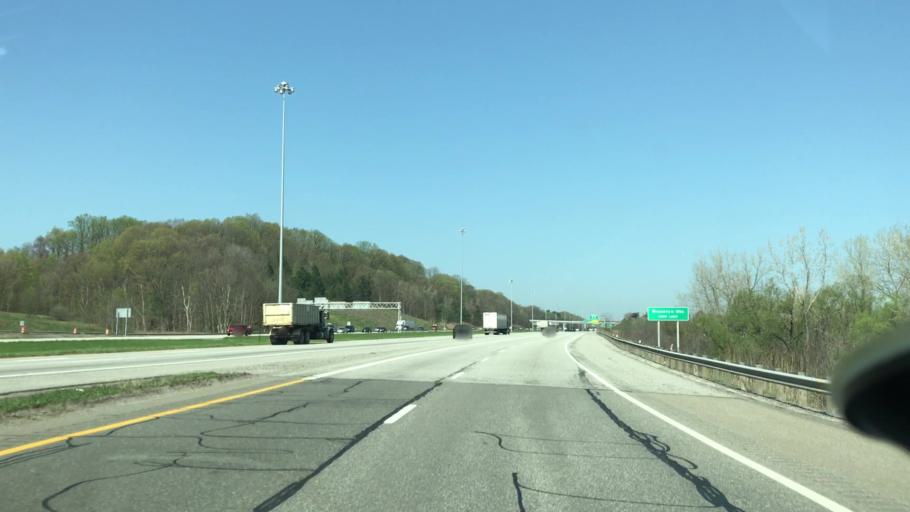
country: US
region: Ohio
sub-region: Cuyahoga County
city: Seven Hills
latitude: 41.4086
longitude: -81.6525
